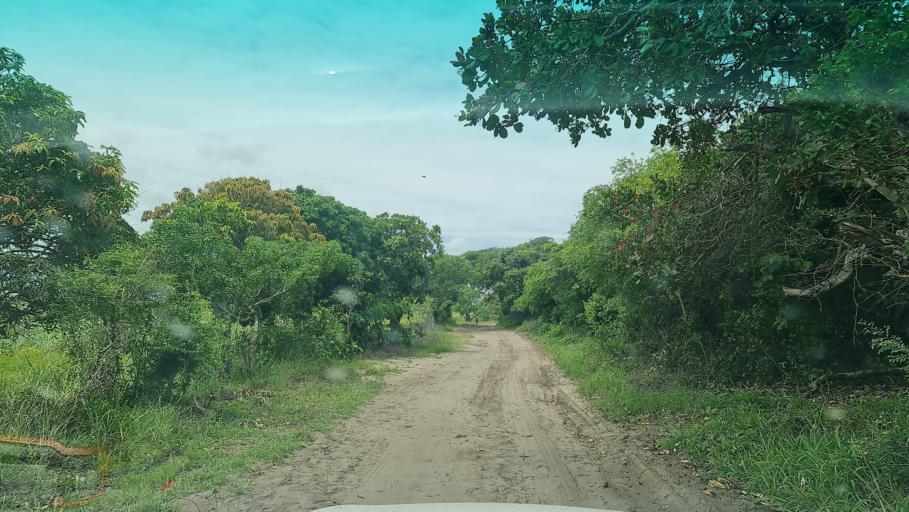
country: MZ
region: Maputo
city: Manhica
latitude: -25.5213
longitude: 32.8629
